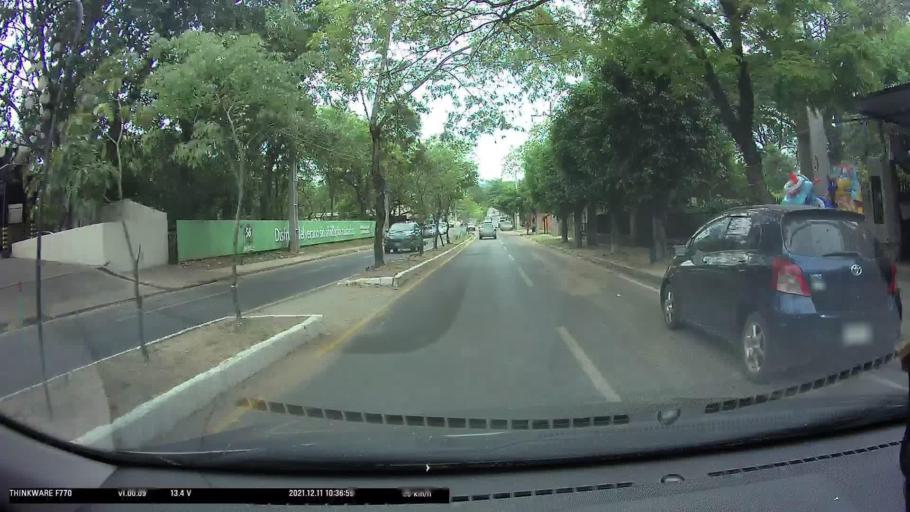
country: PY
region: Cordillera
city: San Bernardino
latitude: -25.3054
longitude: -57.2956
